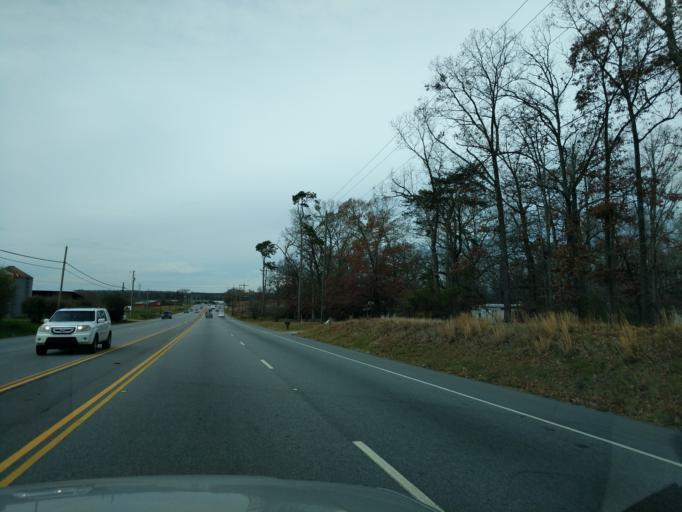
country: US
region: South Carolina
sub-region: Anderson County
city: Northlake
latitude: 34.5814
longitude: -82.7232
